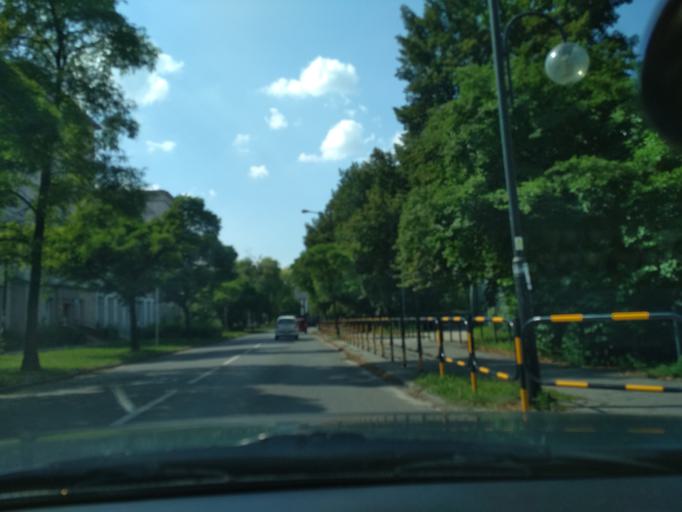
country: PL
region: Silesian Voivodeship
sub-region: Gliwice
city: Gliwice
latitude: 50.2879
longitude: 18.6764
